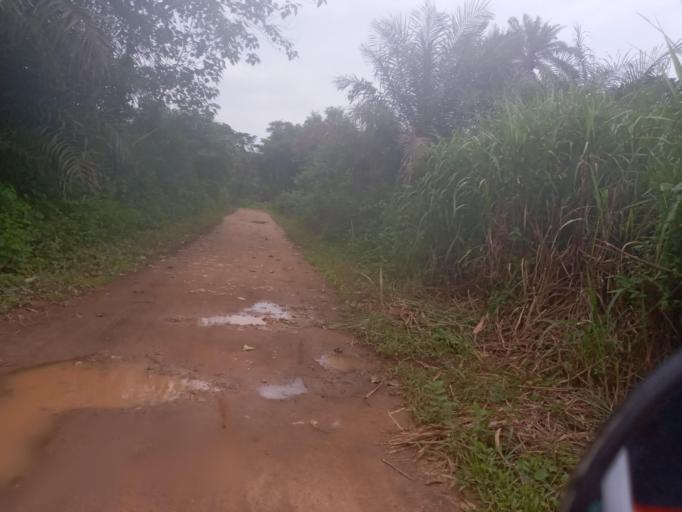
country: SL
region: Northern Province
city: Bumbuna
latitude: 8.9565
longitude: -11.7596
